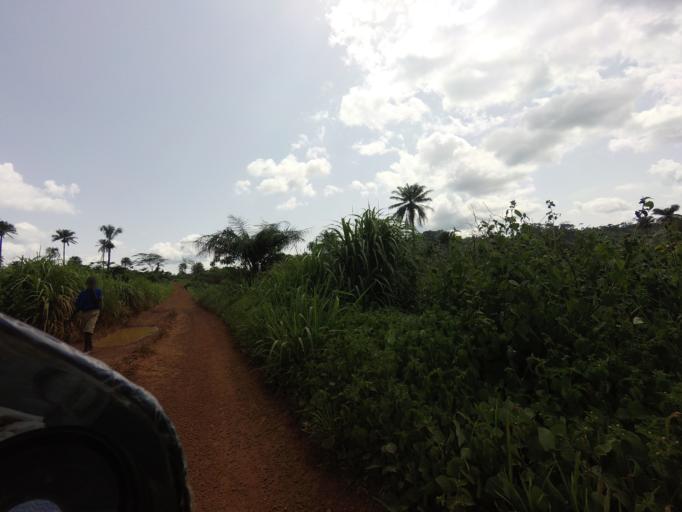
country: SL
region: Eastern Province
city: Manowa
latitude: 8.1400
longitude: -10.7795
